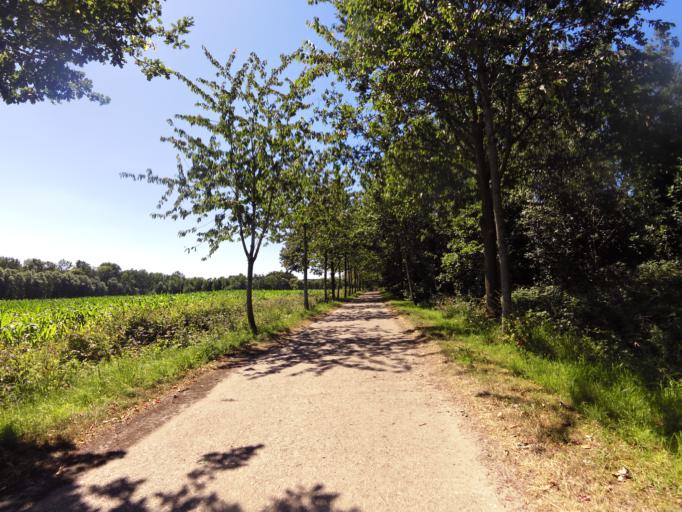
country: BE
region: Flanders
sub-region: Provincie West-Vlaanderen
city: Ichtegem
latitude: 51.0772
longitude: 3.0557
